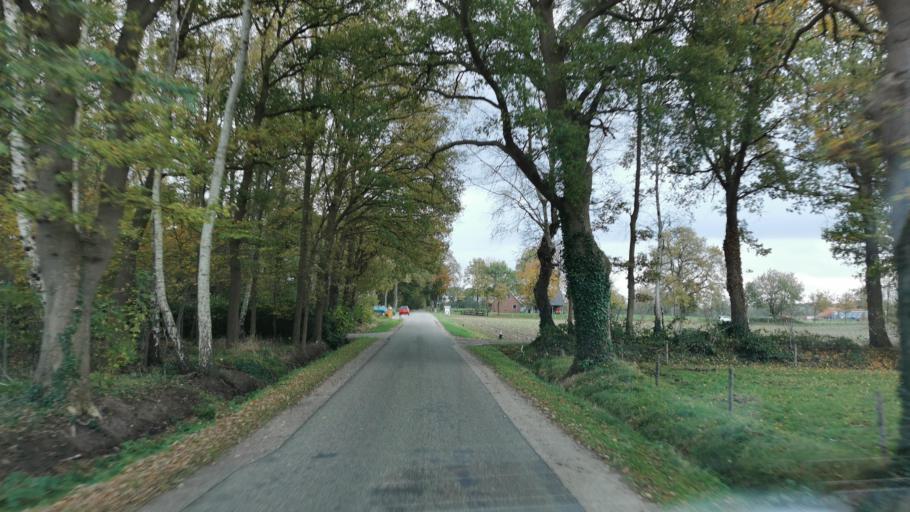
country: NL
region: Overijssel
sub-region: Gemeente Losser
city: Losser
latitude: 52.2496
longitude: 7.0375
